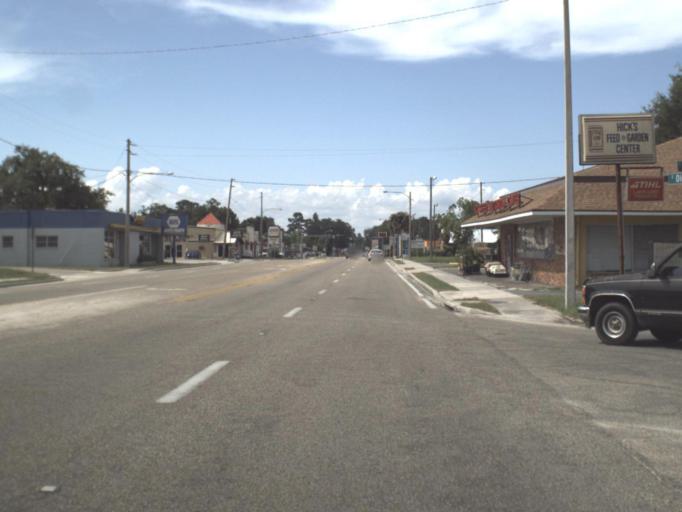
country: US
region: Florida
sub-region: Taylor County
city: Perry
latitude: 30.1091
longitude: -83.5820
